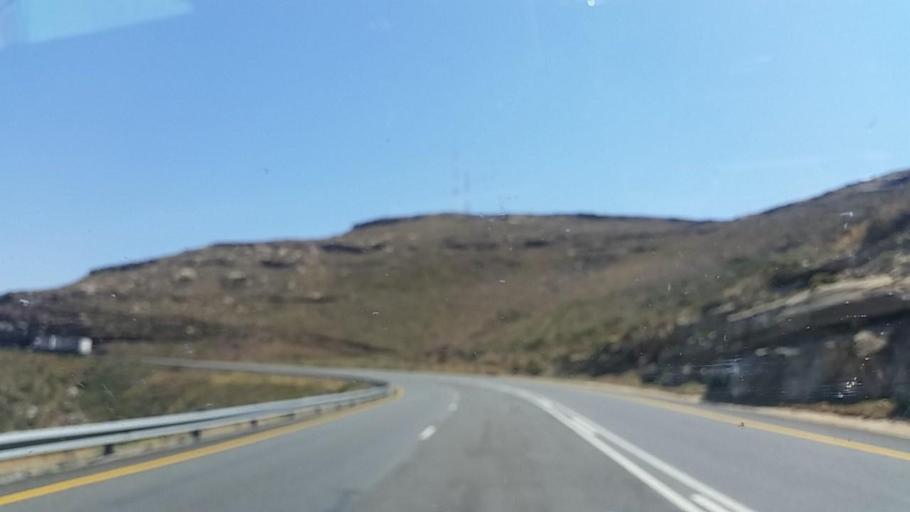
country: ZA
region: Eastern Cape
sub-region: Chris Hani District Municipality
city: Middelburg
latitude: -31.8402
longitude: 24.8661
